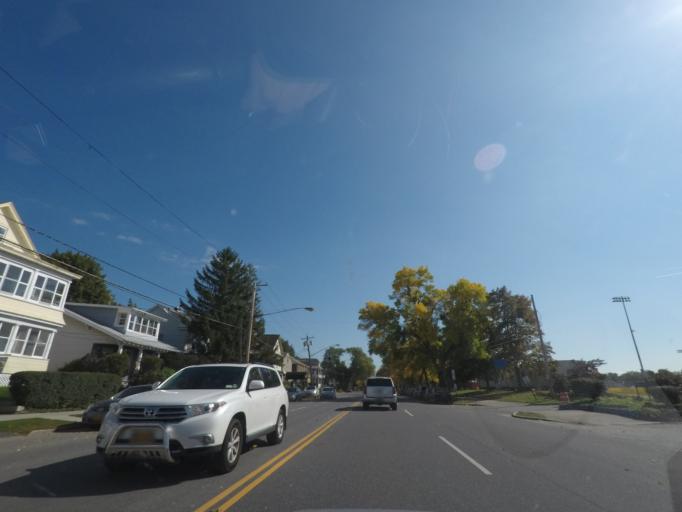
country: US
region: New York
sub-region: Albany County
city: West Albany
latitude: 42.6673
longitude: -73.7816
